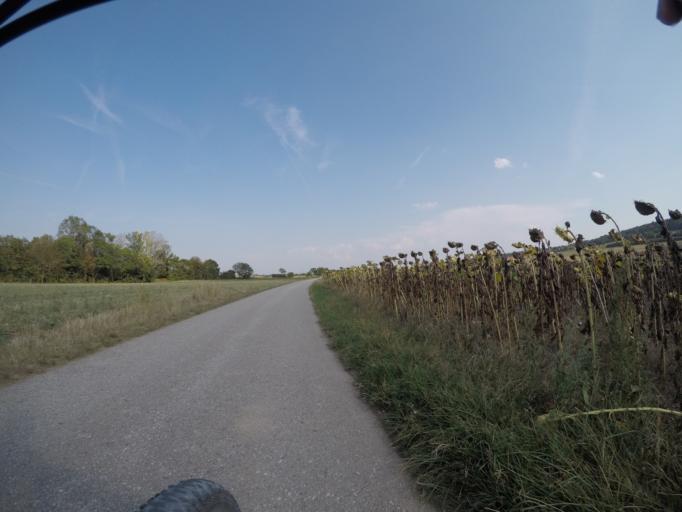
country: AT
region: Lower Austria
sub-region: Politischer Bezirk Baden
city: Hirtenberg
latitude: 47.9625
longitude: 16.1577
